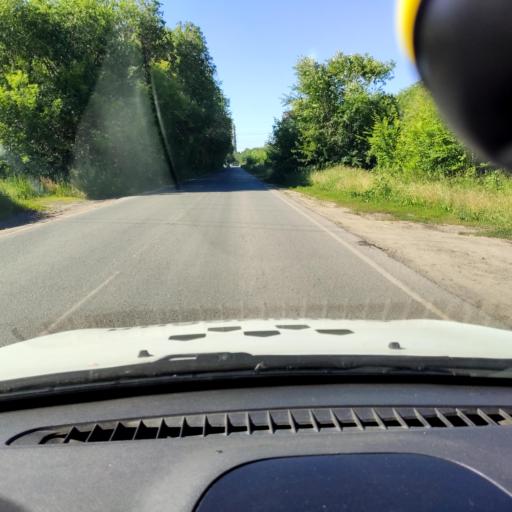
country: RU
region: Samara
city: Tol'yatti
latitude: 53.5813
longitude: 49.2562
